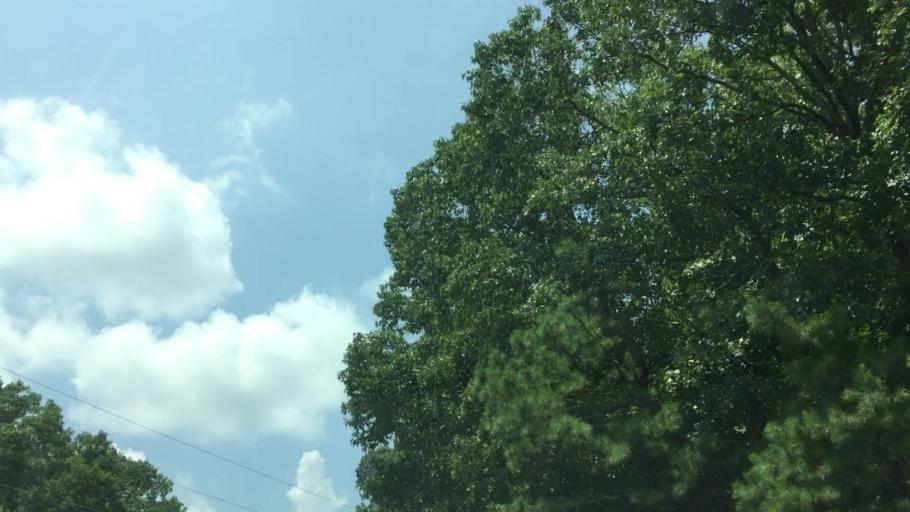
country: US
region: Georgia
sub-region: Carroll County
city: Carrollton
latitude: 33.6140
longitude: -84.9813
